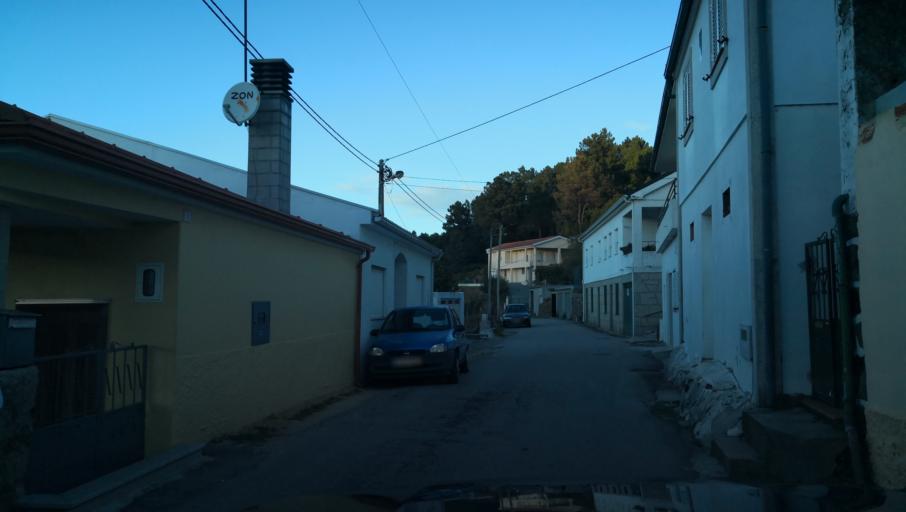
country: PT
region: Vila Real
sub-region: Santa Marta de Penaguiao
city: Santa Marta de Penaguiao
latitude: 41.2560
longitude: -7.7866
